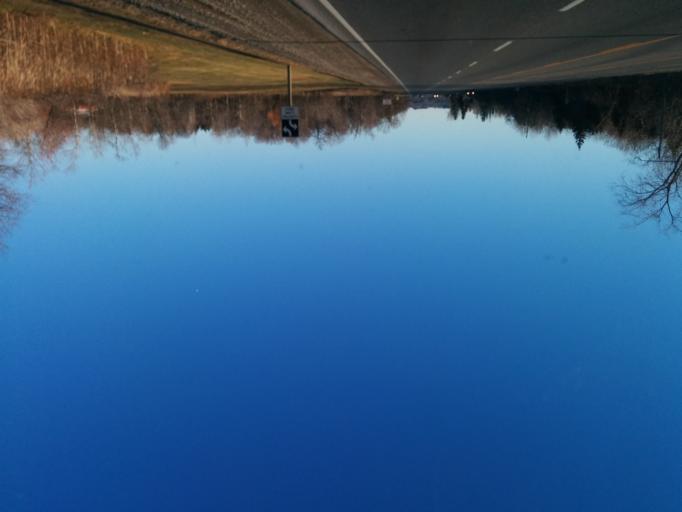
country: CA
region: Ontario
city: Brampton
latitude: 43.8018
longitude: -79.9167
